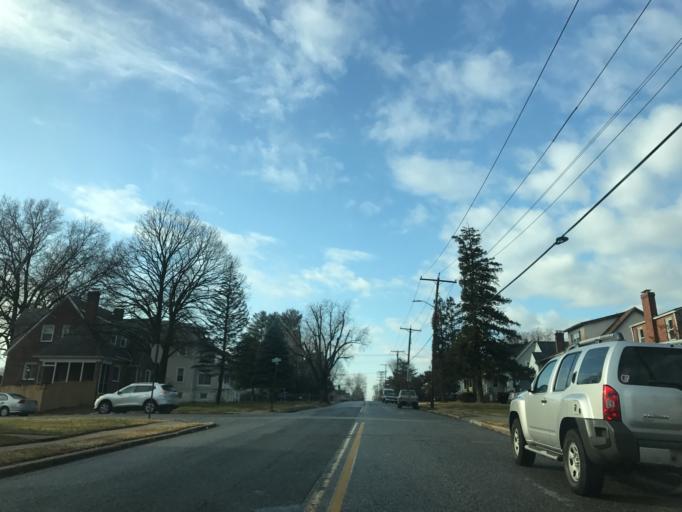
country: US
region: Maryland
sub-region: Baltimore County
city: Parkville
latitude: 39.3541
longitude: -76.5484
